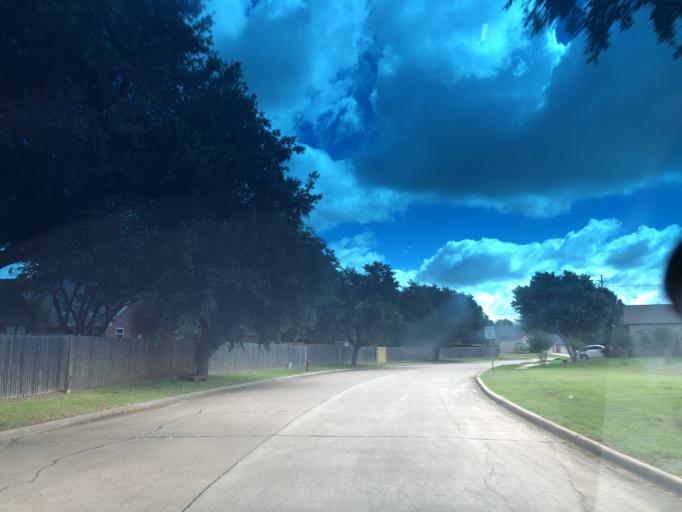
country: US
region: Texas
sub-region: Dallas County
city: Grand Prairie
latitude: 32.6951
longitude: -97.0373
